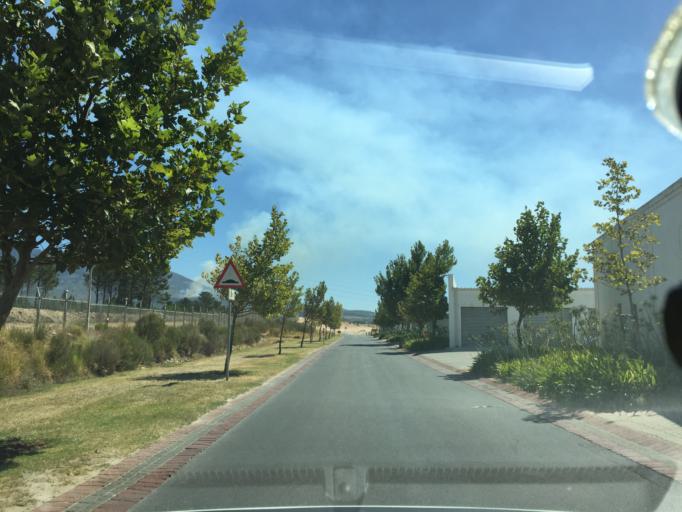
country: ZA
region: Western Cape
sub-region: Cape Winelands District Municipality
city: Paarl
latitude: -33.8084
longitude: 18.9759
